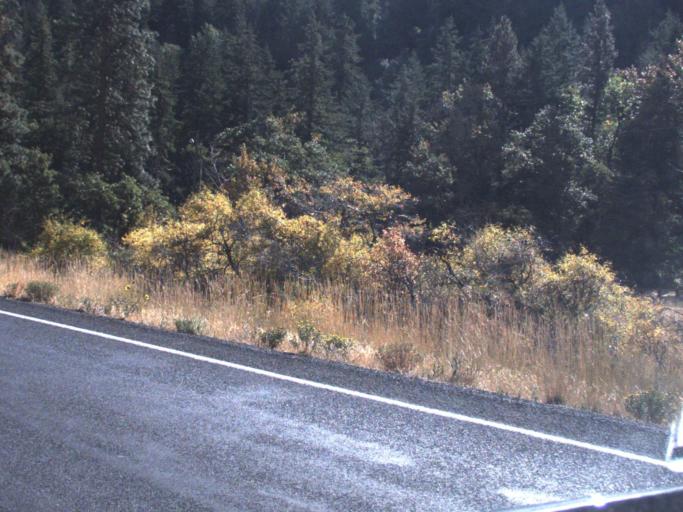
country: US
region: Washington
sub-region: Yakima County
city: Tieton
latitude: 46.6938
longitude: -120.9069
